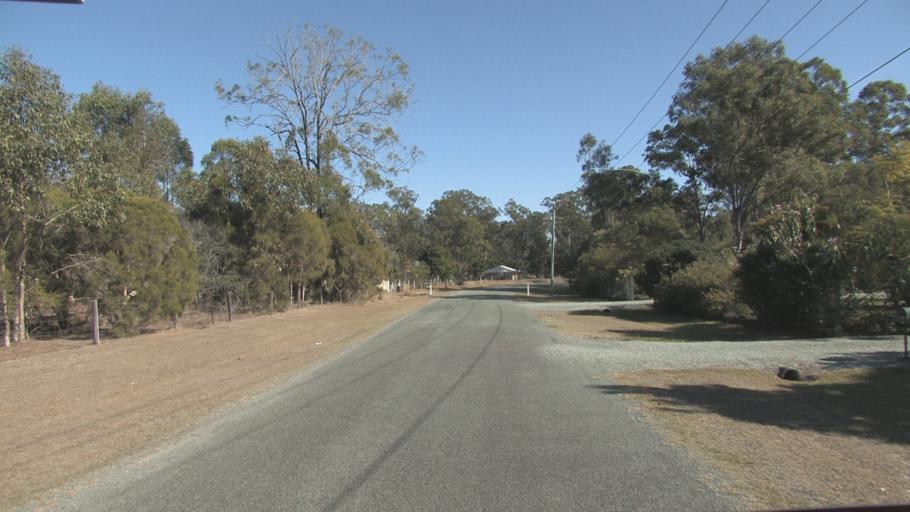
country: AU
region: Queensland
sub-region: Logan
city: Cedar Vale
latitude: -27.8318
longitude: 153.0449
